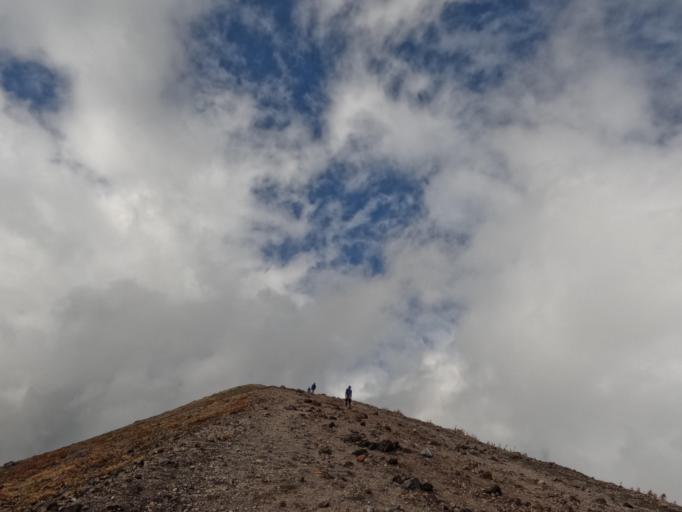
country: JP
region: Hokkaido
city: Shiraoi
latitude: 42.6906
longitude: 141.3871
